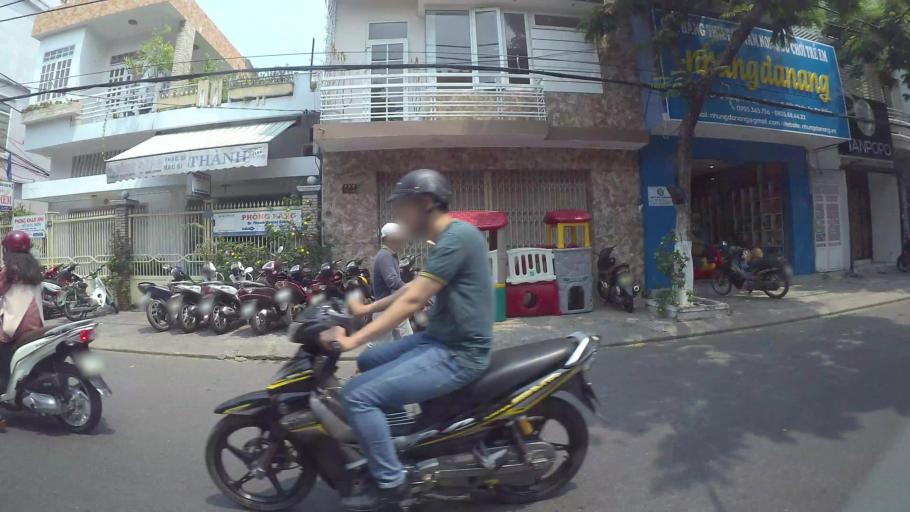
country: VN
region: Da Nang
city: Da Nang
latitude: 16.0773
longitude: 108.2154
